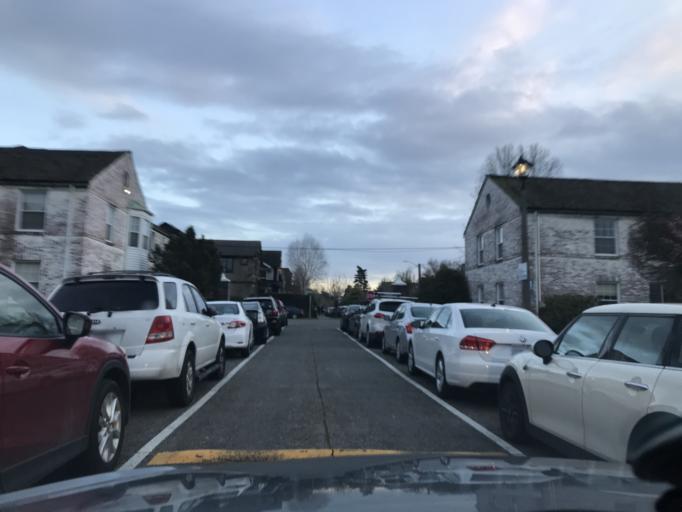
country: US
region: Washington
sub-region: King County
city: Medina
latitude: 47.6412
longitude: -122.2795
